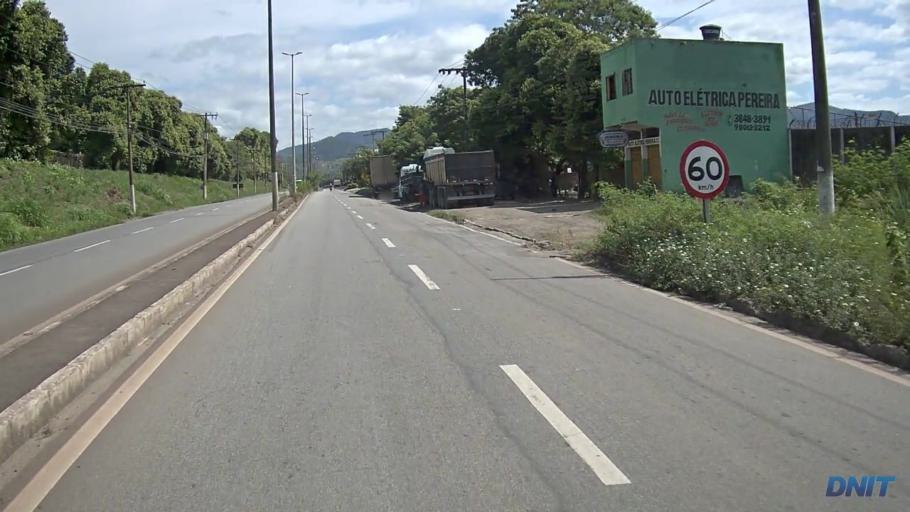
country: BR
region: Minas Gerais
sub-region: Coronel Fabriciano
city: Coronel Fabriciano
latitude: -19.5281
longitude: -42.6441
